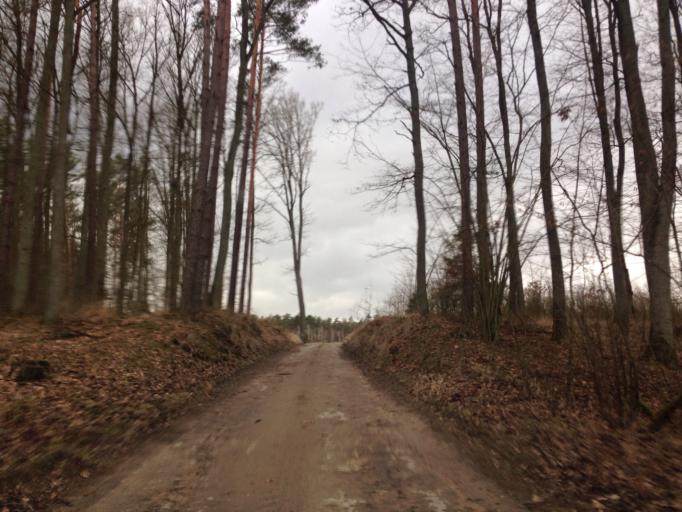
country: PL
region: Kujawsko-Pomorskie
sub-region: Powiat brodnicki
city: Gorzno
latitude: 53.1749
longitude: 19.6866
